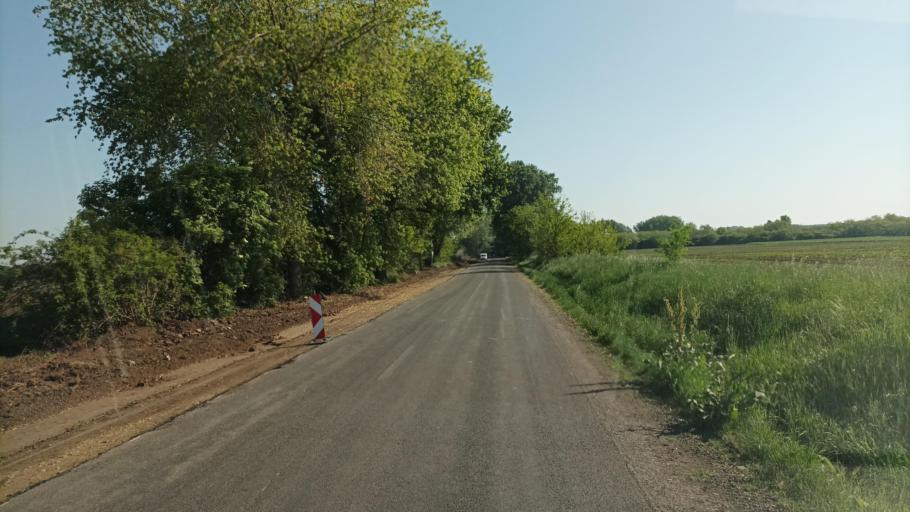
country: HU
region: Pest
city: Nyaregyhaza
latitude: 47.2994
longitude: 19.5006
